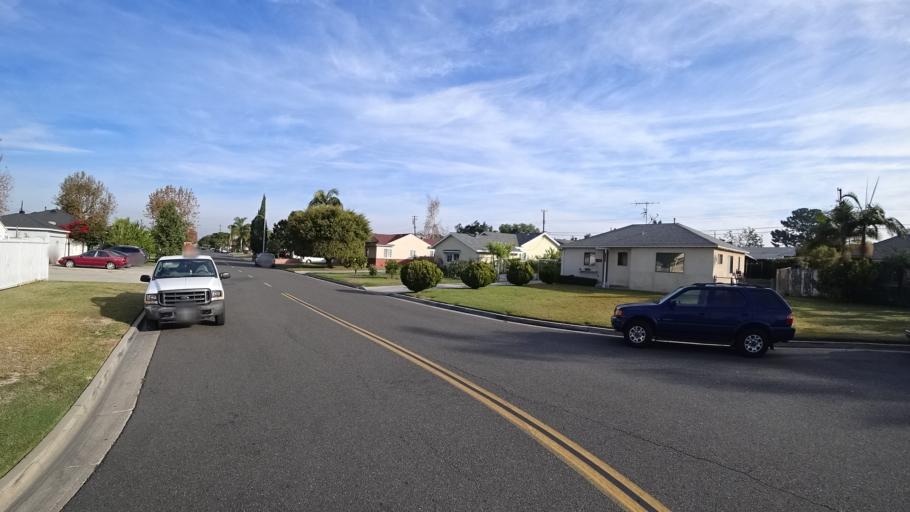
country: US
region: California
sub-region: Orange County
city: Garden Grove
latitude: 33.7916
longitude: -117.9274
